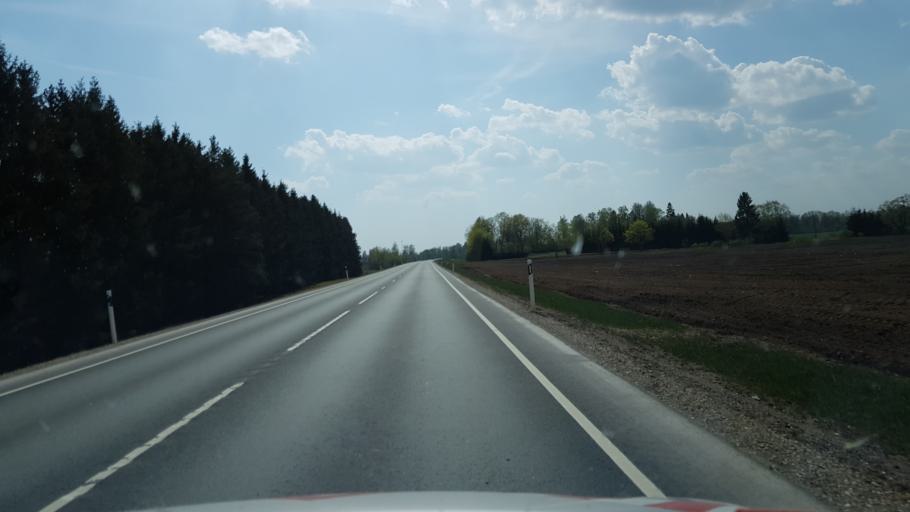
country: EE
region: Paernumaa
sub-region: Tootsi vald
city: Tootsi
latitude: 58.5422
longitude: 24.8424
